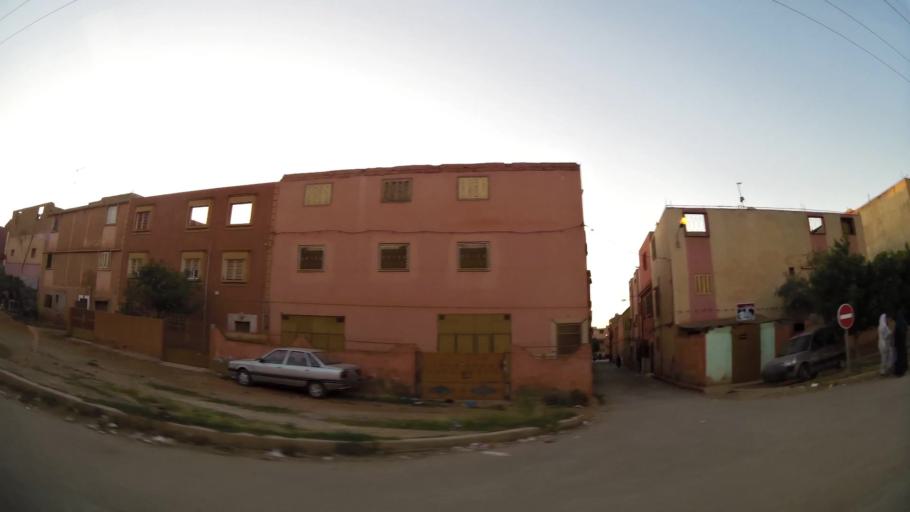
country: MA
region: Oriental
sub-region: Berkane-Taourirt
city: Berkane
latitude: 34.9201
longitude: -2.3150
